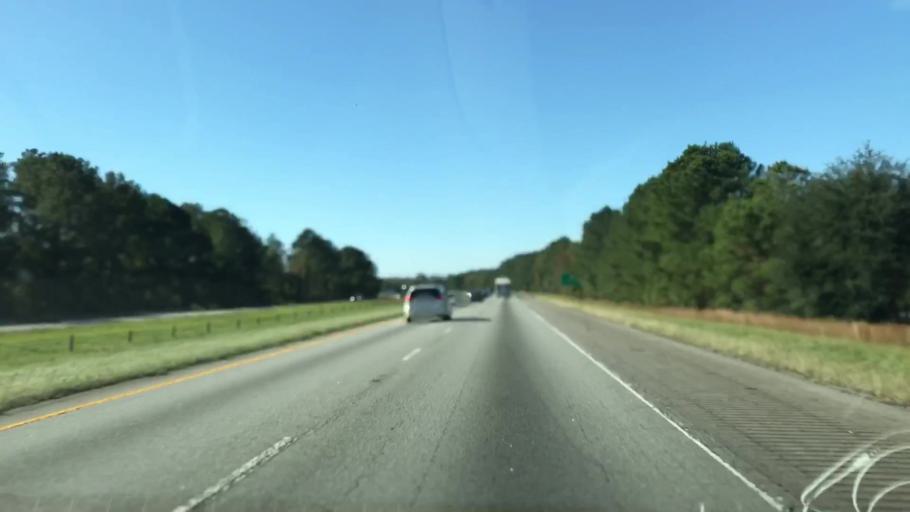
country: US
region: South Carolina
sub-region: Hampton County
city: Yemassee
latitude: 32.5937
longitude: -80.9164
